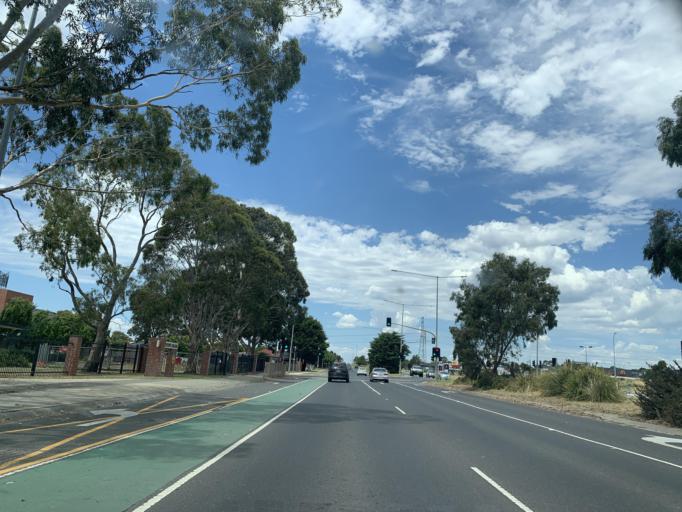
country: AU
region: Victoria
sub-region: Casey
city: Cranbourne West
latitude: -38.1098
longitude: 145.2574
